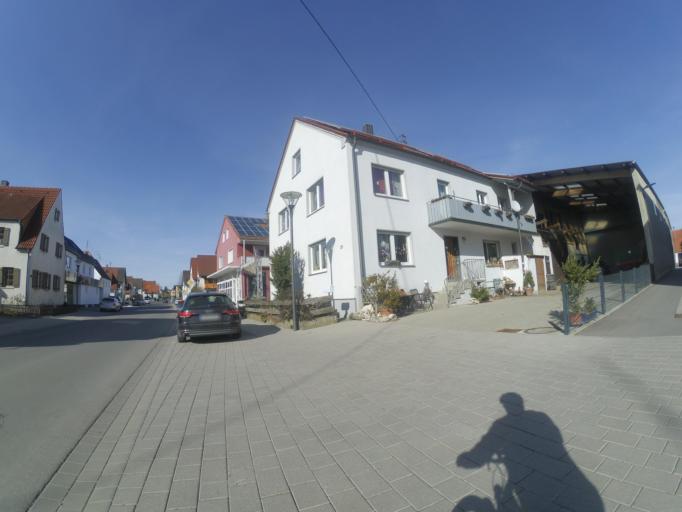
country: DE
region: Baden-Wuerttemberg
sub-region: Regierungsbezirk Stuttgart
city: Sontheim an der Brenz
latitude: 48.5549
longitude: 10.2882
